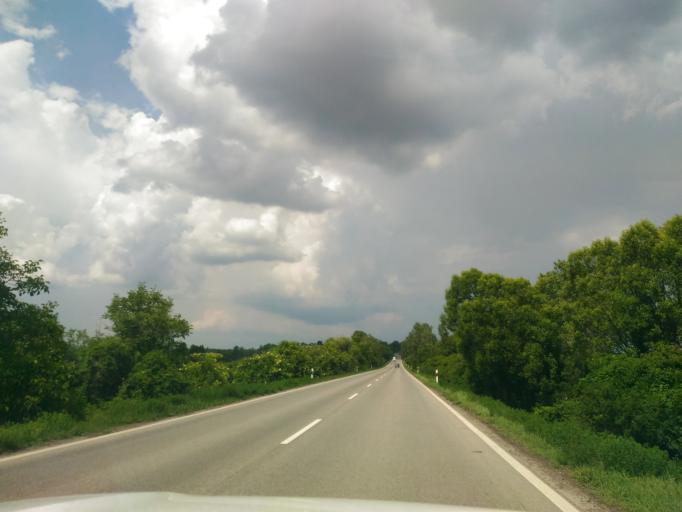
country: HU
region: Baranya
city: Hidas
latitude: 46.2673
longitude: 18.5124
